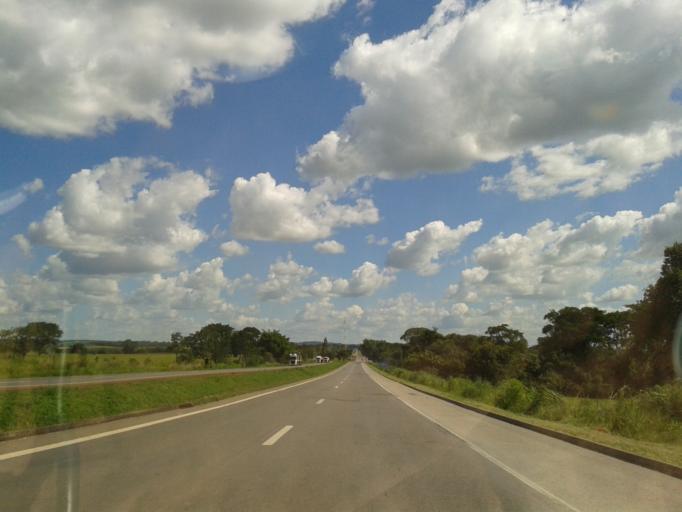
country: BR
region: Goias
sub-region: Morrinhos
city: Morrinhos
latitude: -17.6192
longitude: -49.1800
